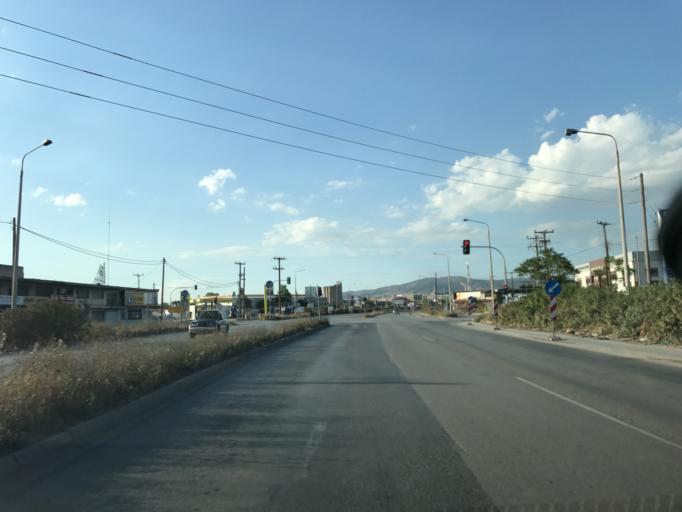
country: GR
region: Central Macedonia
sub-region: Nomos Thessalonikis
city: Menemeni
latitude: 40.6627
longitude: 22.8817
